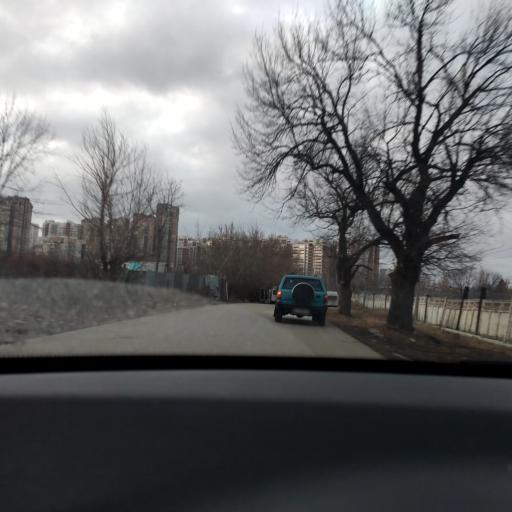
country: RU
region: Samara
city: Samara
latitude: 53.2481
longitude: 50.1813
